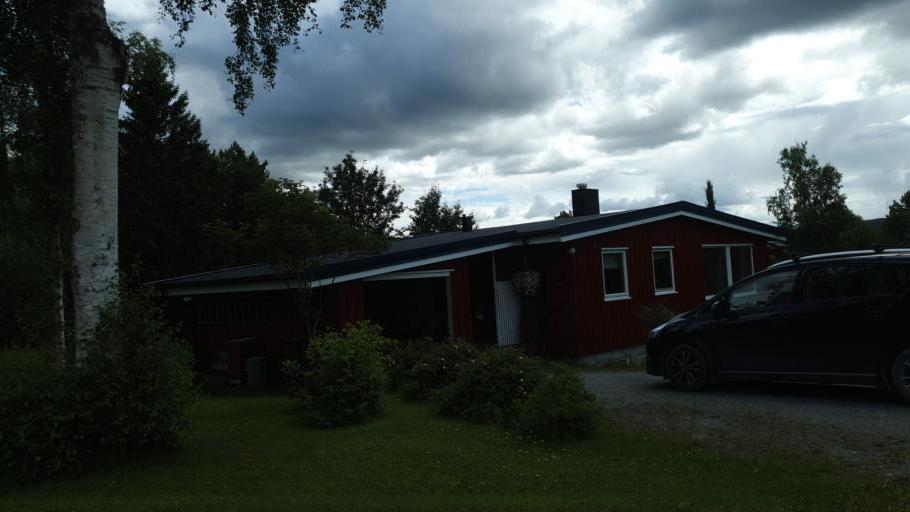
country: NO
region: Sor-Trondelag
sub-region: Rennebu
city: Berkak
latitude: 62.8331
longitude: 10.0046
